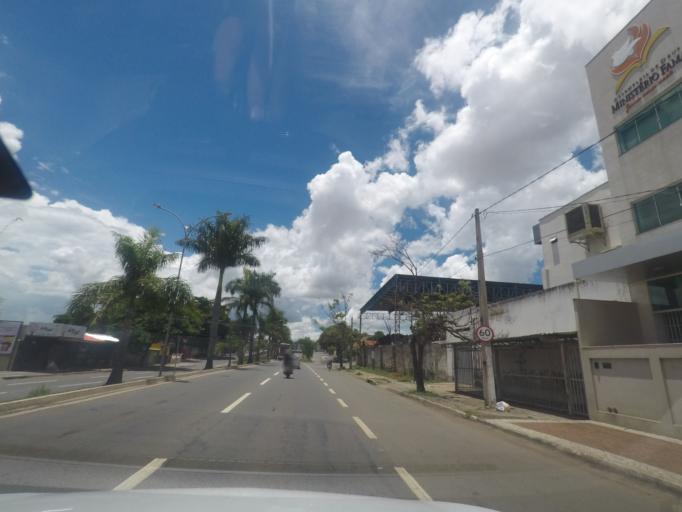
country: BR
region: Goias
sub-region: Goiania
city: Goiania
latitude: -16.6640
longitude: -49.2819
